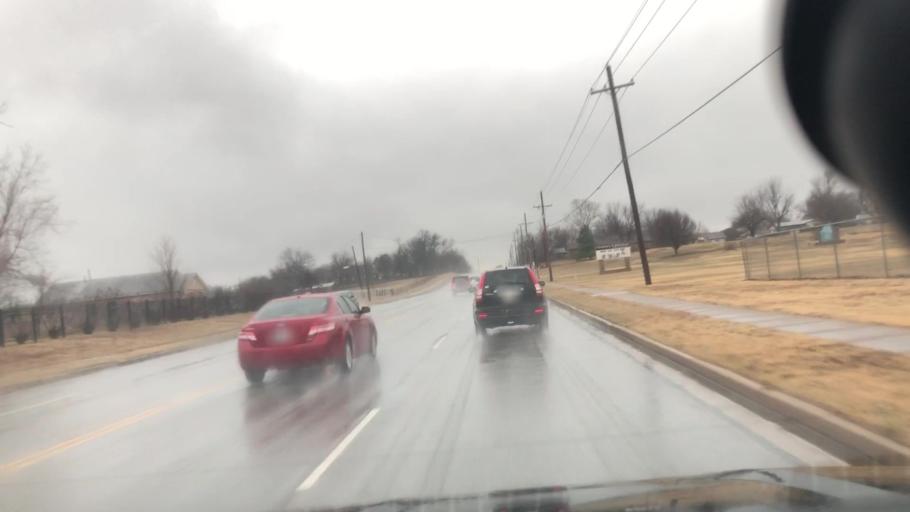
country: US
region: Oklahoma
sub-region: Rogers County
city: Catoosa
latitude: 36.1458
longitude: -95.8333
